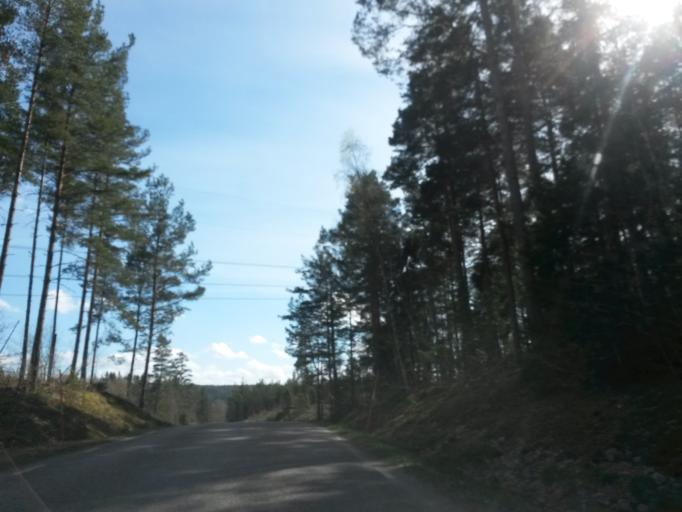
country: SE
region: Vaestra Goetaland
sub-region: Vargarda Kommun
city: Jonstorp
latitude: 57.9912
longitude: 12.7690
